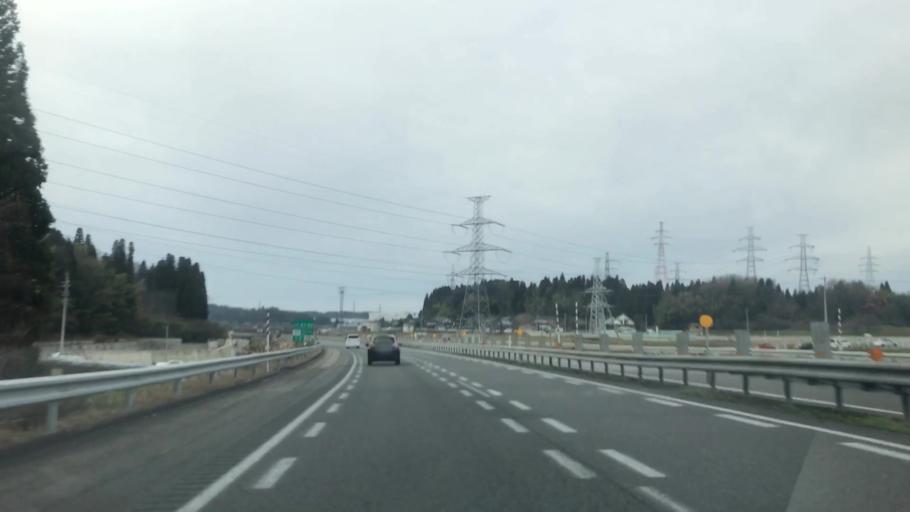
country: JP
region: Toyama
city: Kuragaki-kosugi
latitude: 36.6928
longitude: 137.0918
